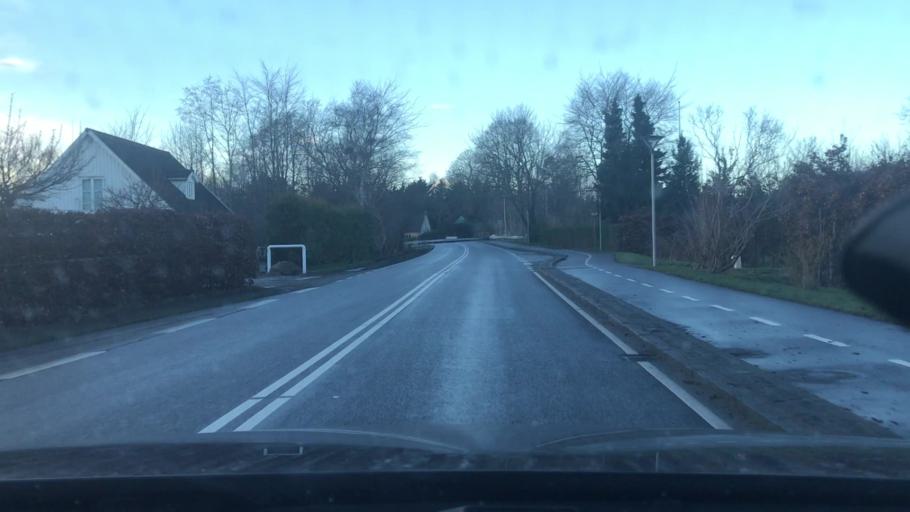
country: DK
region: Zealand
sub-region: Solrod Kommune
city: Havdrup
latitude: 55.5151
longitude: 12.1472
